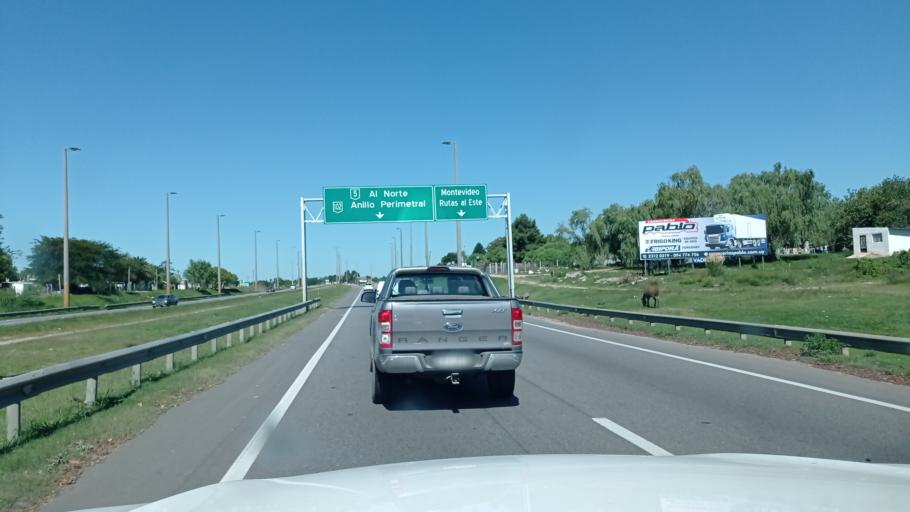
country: UY
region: Montevideo
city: Montevideo
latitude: -34.8546
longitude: -56.2623
